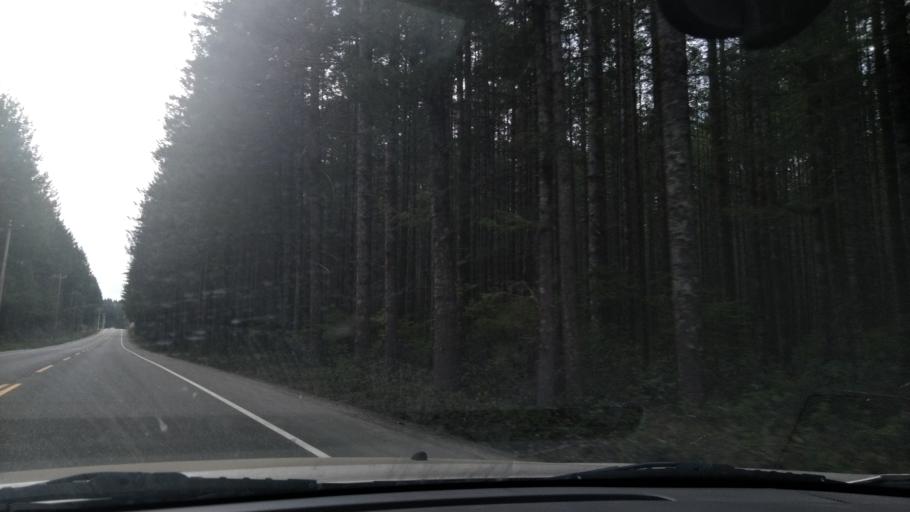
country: CA
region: British Columbia
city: Campbell River
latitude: 50.0323
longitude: -125.3383
